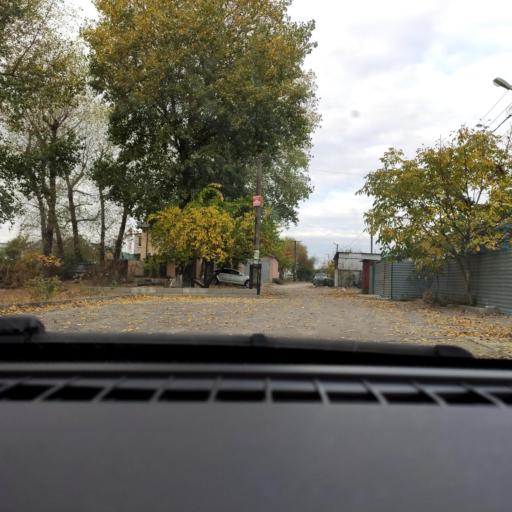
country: RU
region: Voronezj
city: Maslovka
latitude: 51.6320
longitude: 39.2696
